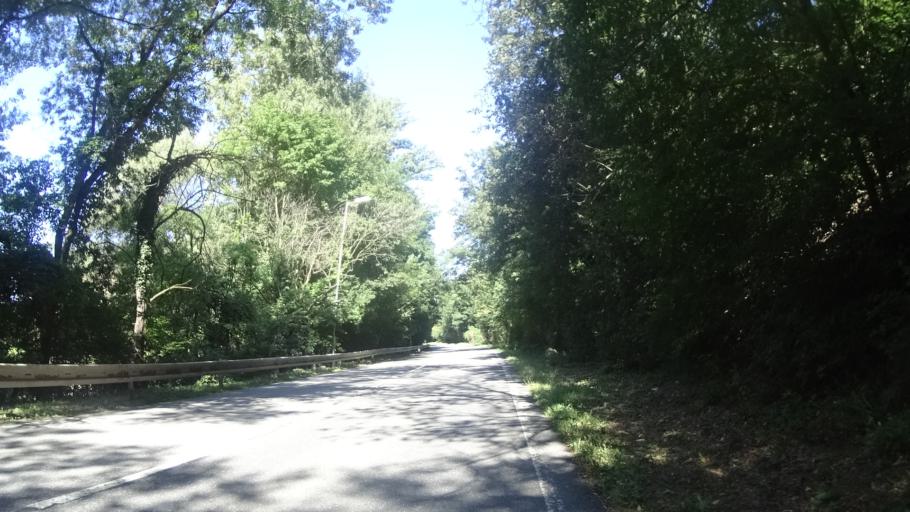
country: AT
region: Lower Austria
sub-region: Politischer Bezirk Bruck an der Leitha
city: Wolfsthal
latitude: 48.1558
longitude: 17.0173
